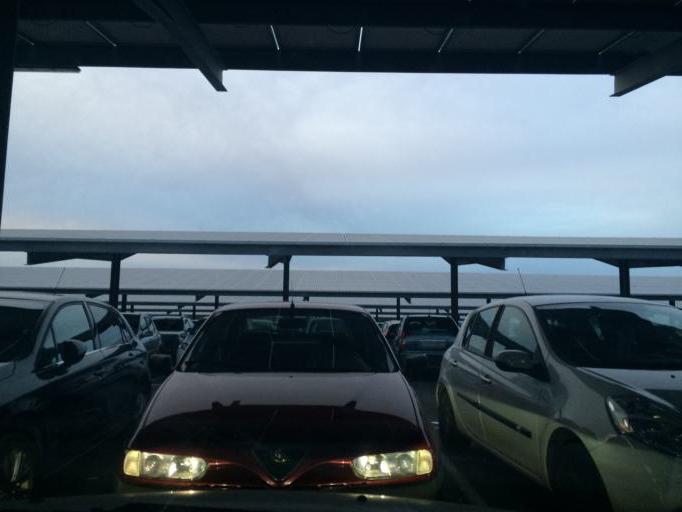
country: ES
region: Andalusia
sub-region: Provincia de Almeria
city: Almeria
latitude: 36.8317
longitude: -2.4017
